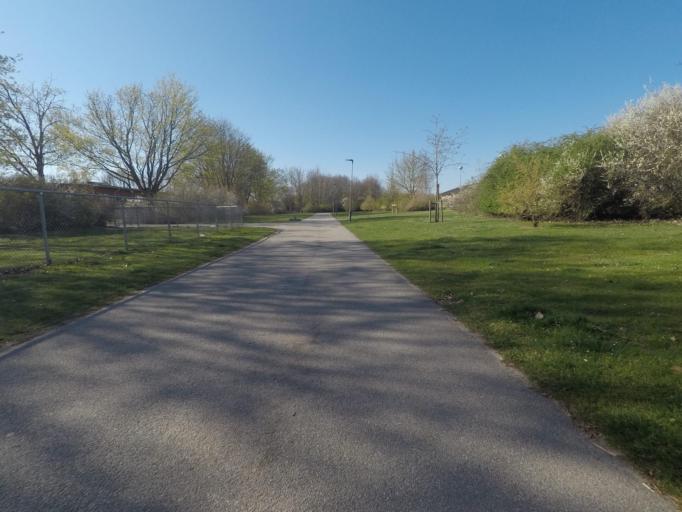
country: SE
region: Skane
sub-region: Malmo
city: Tygelsjo
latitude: 55.5572
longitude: 13.0125
